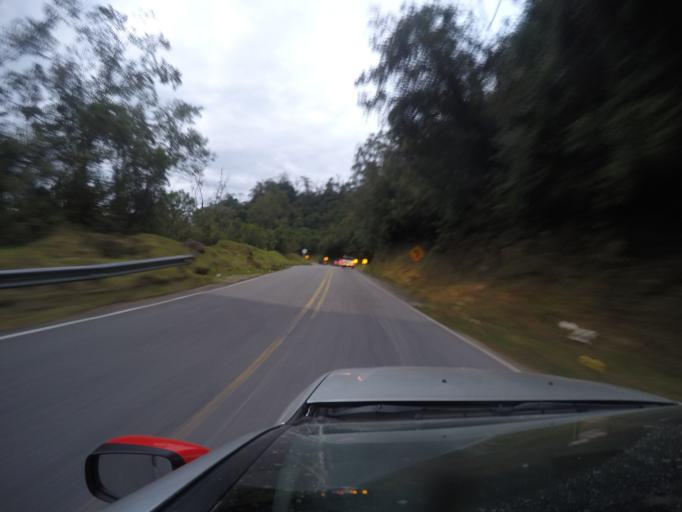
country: CO
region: Tolima
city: Herveo
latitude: 5.1351
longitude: -75.1682
